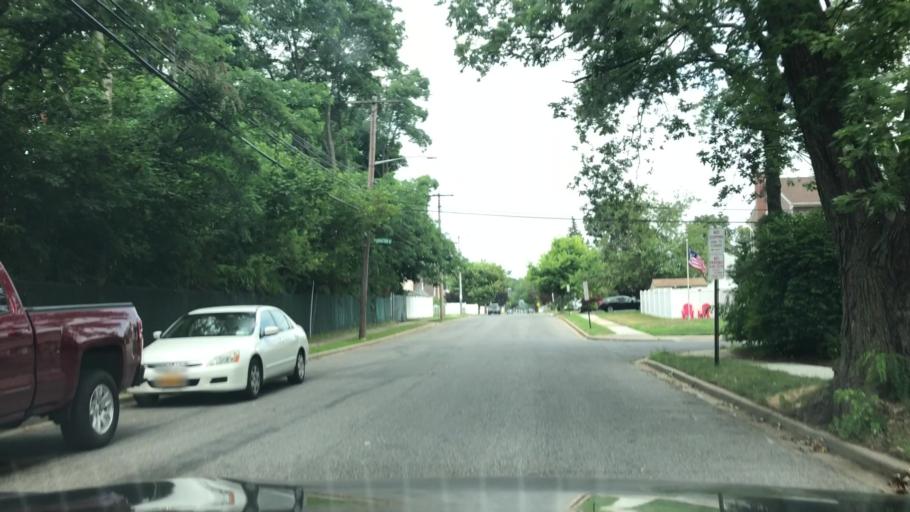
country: US
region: New York
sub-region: Nassau County
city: North Massapequa
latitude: 40.6929
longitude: -73.4677
